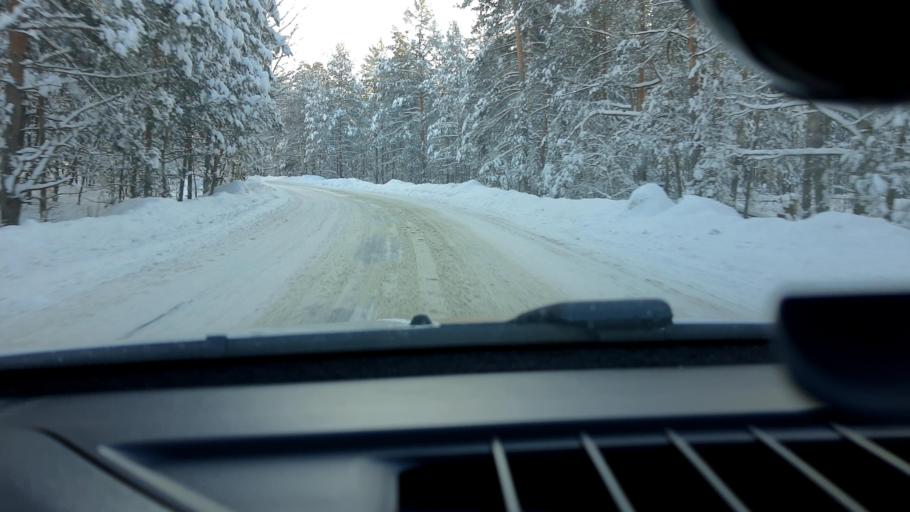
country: RU
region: Nizjnij Novgorod
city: Babino
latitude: 56.3298
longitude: 43.6244
